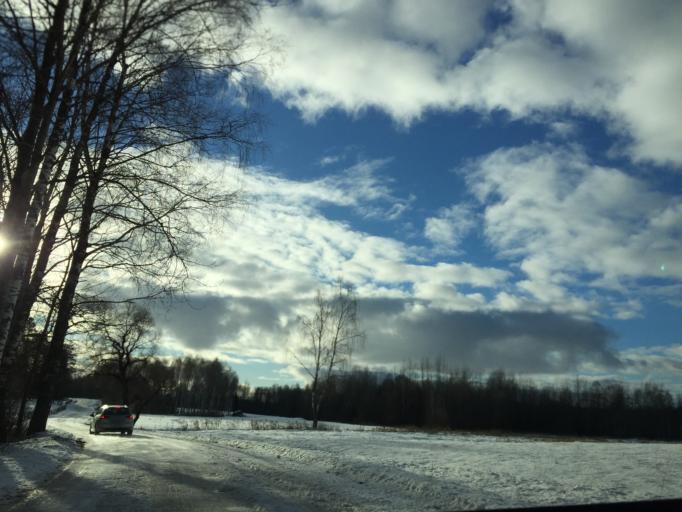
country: LV
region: Lielvarde
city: Lielvarde
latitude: 56.5712
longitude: 24.7985
